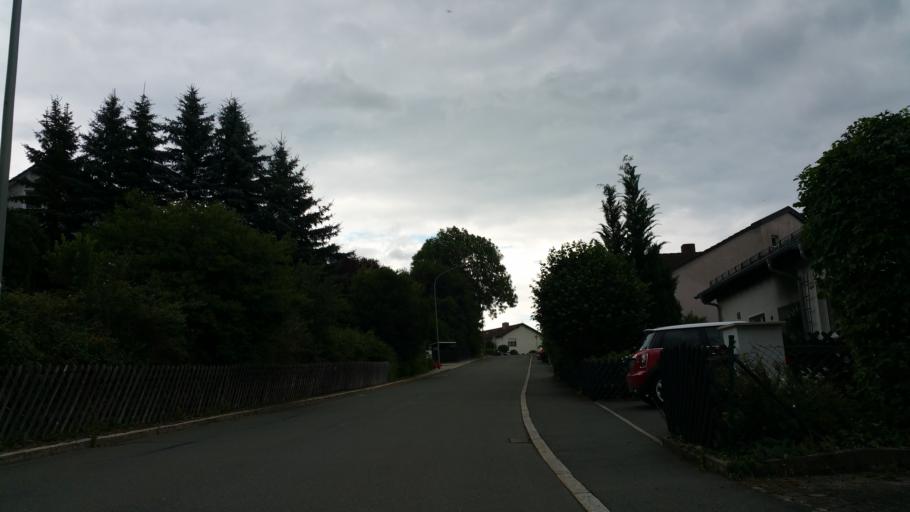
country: DE
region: Bavaria
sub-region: Upper Franconia
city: Oberkotzau
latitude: 50.2579
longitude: 11.9389
